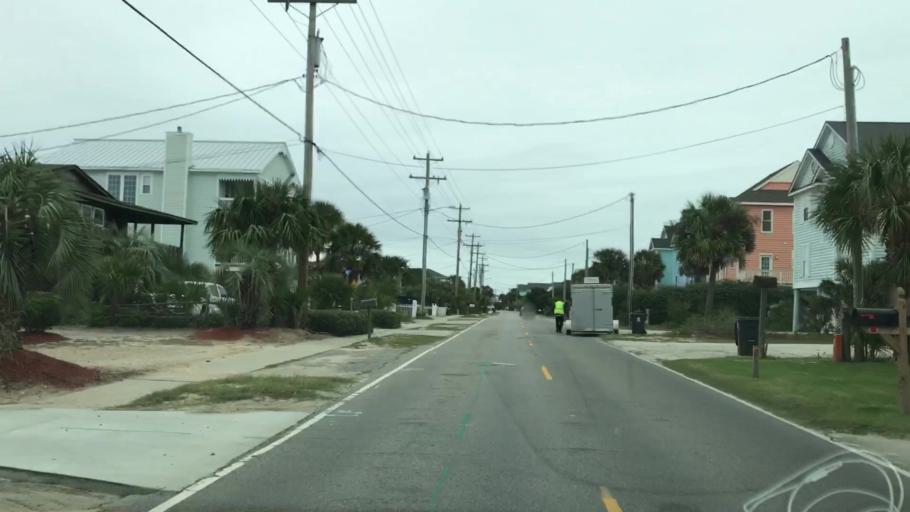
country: US
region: South Carolina
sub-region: Horry County
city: Garden City
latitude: 33.5643
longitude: -79.0097
